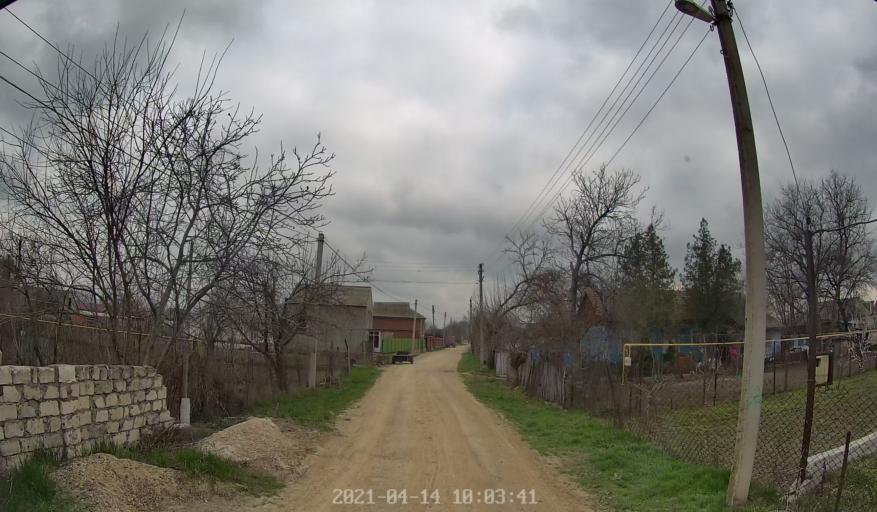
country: MD
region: Chisinau
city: Vadul lui Voda
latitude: 47.1438
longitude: 29.1250
